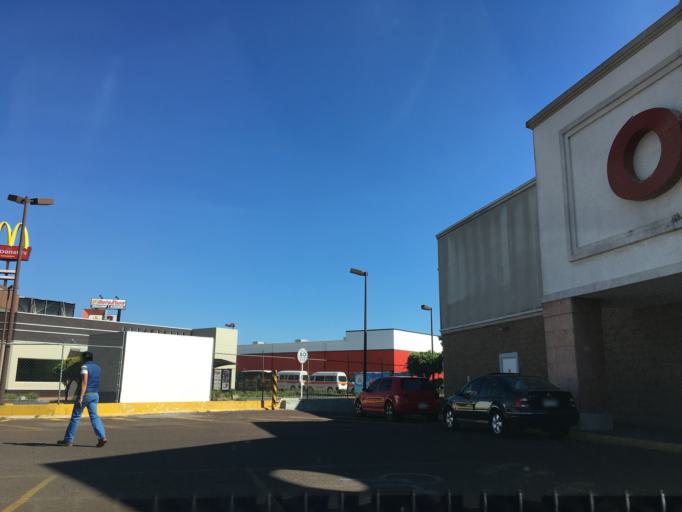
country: MX
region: Michoacan
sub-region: Morelia
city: Morelos
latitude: 19.6792
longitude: -101.2178
